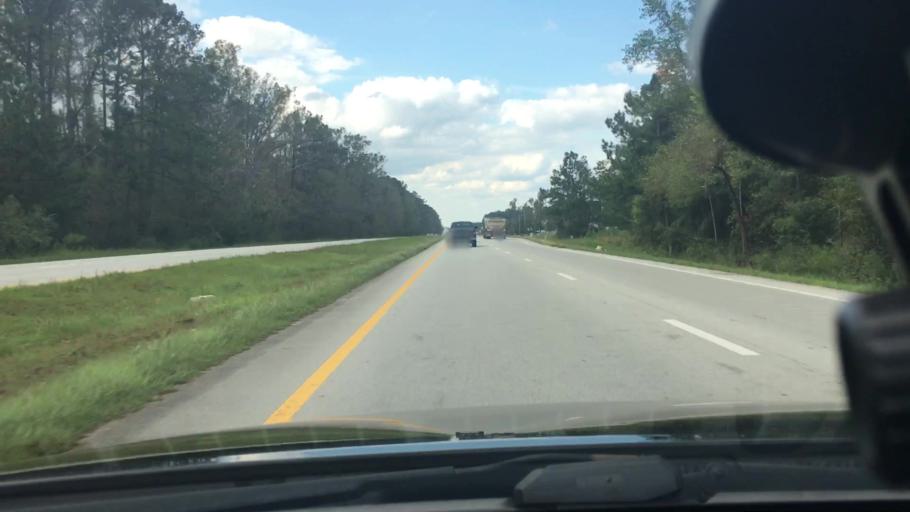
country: US
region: North Carolina
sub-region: Craven County
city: Fairfield Harbour
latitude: 35.0260
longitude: -77.0006
